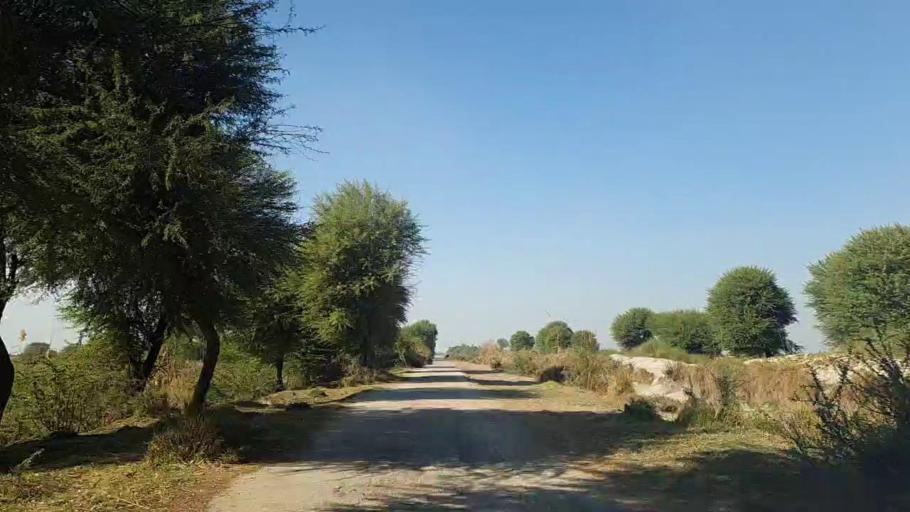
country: PK
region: Sindh
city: Shahpur Chakar
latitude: 26.2160
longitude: 68.6063
